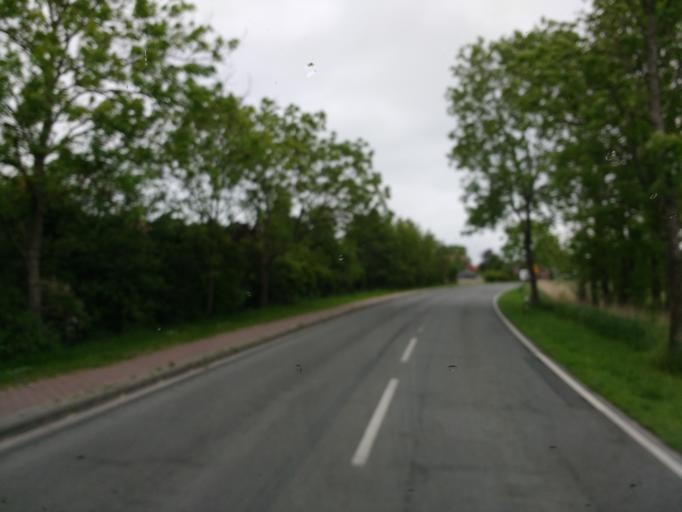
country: DE
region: Lower Saxony
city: Jever
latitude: 53.6335
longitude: 7.9225
